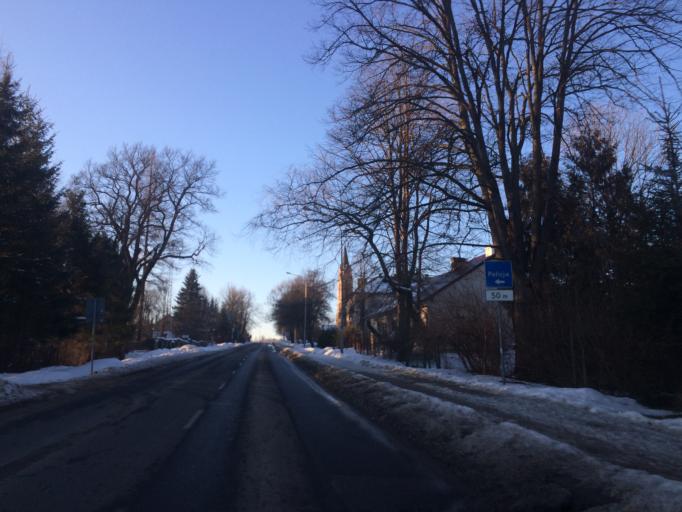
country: PL
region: Subcarpathian Voivodeship
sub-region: Powiat bieszczadzki
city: Lutowiska
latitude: 49.2525
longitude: 22.6934
